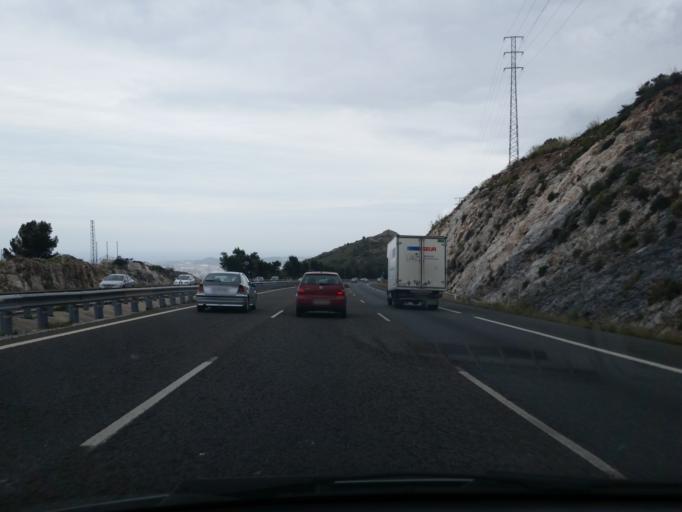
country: ES
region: Andalusia
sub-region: Provincia de Malaga
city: Benalmadena
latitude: 36.5924
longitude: -4.5805
